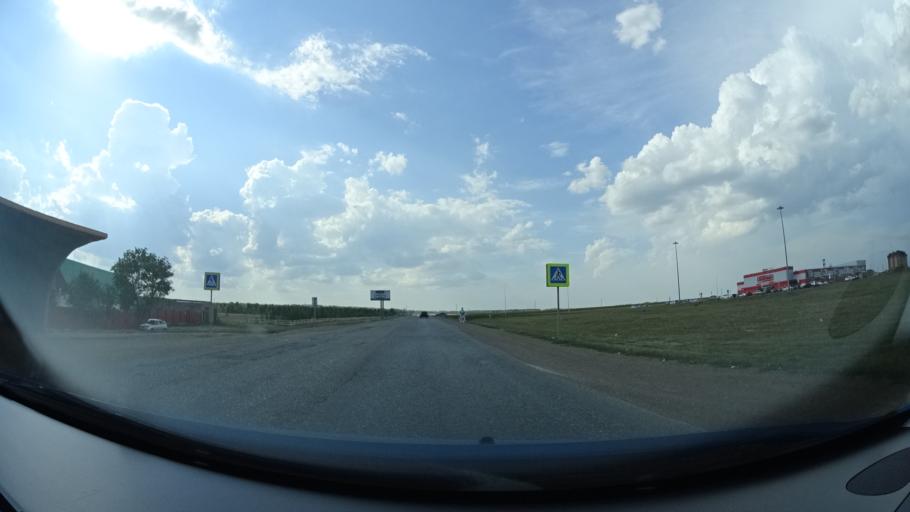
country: RU
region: Bashkortostan
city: Meleuz
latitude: 52.9645
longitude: 55.9097
